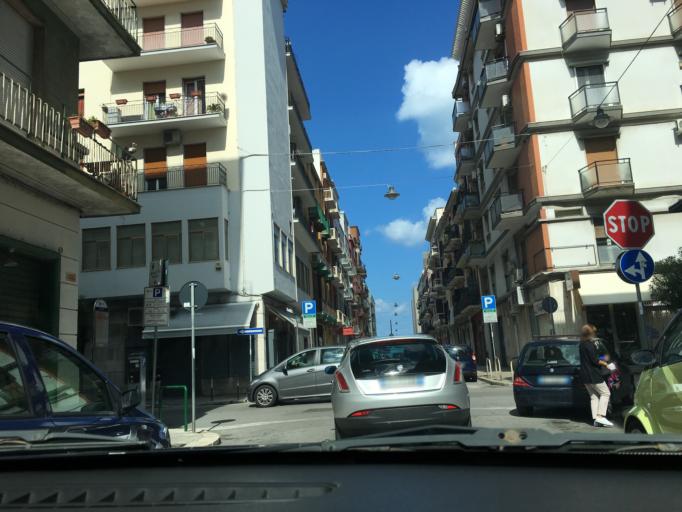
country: IT
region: Apulia
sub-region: Provincia di Bari
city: Bari
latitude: 41.1193
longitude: 16.8817
